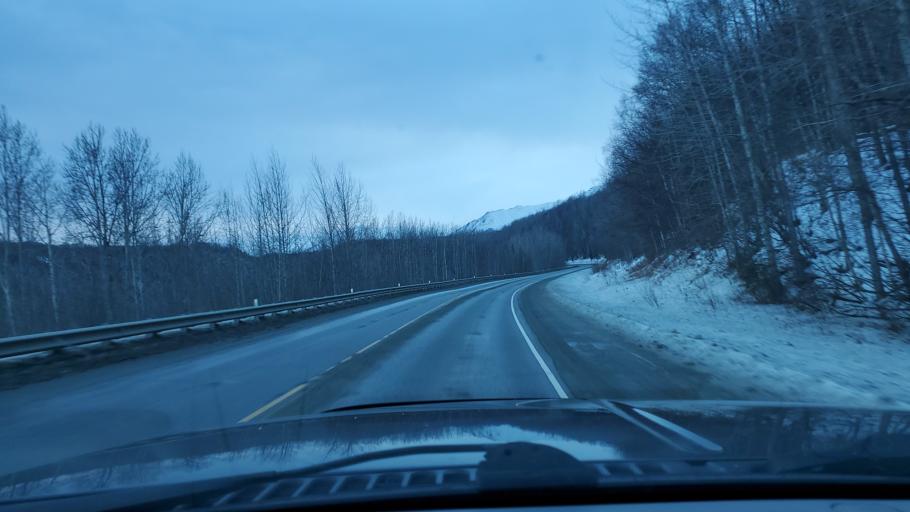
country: US
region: Alaska
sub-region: Matanuska-Susitna Borough
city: Lazy Mountain
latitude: 61.6790
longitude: -149.0294
